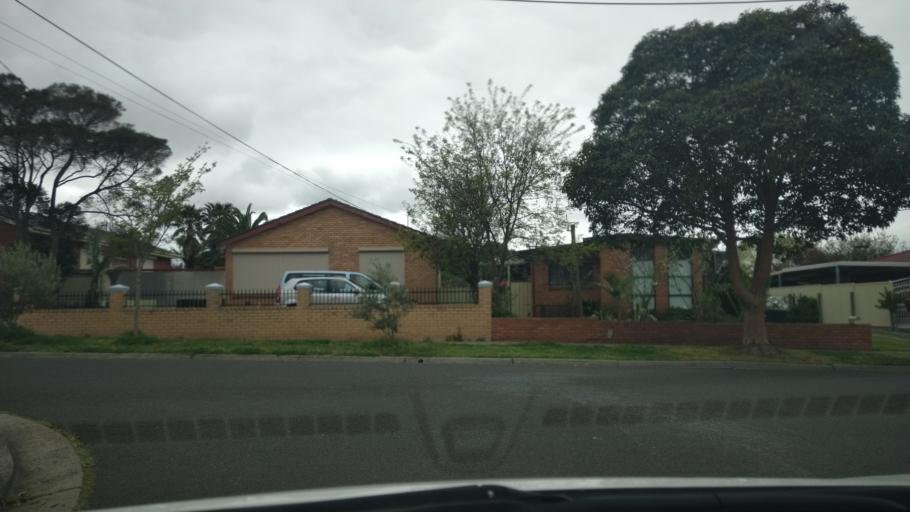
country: AU
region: Victoria
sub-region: Greater Dandenong
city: Keysborough
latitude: -37.9926
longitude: 145.1831
